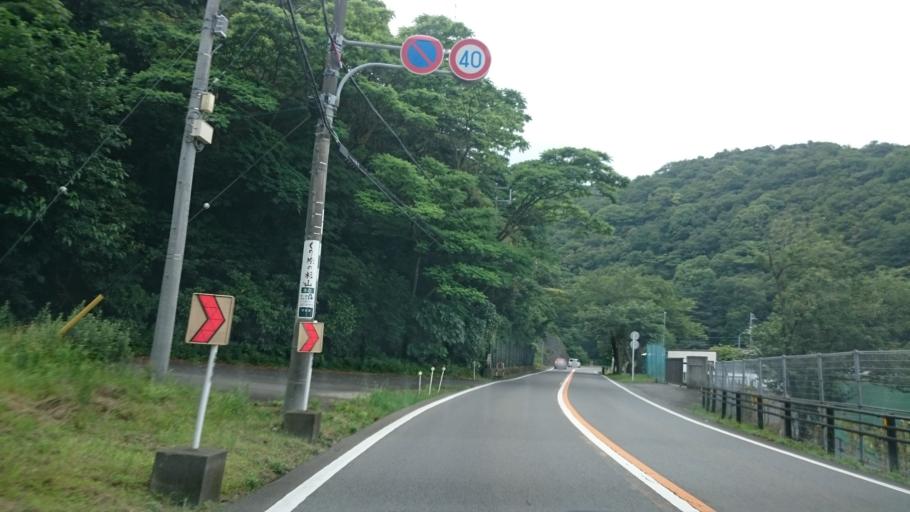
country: JP
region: Shizuoka
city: Ito
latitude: 35.0263
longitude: 139.0970
